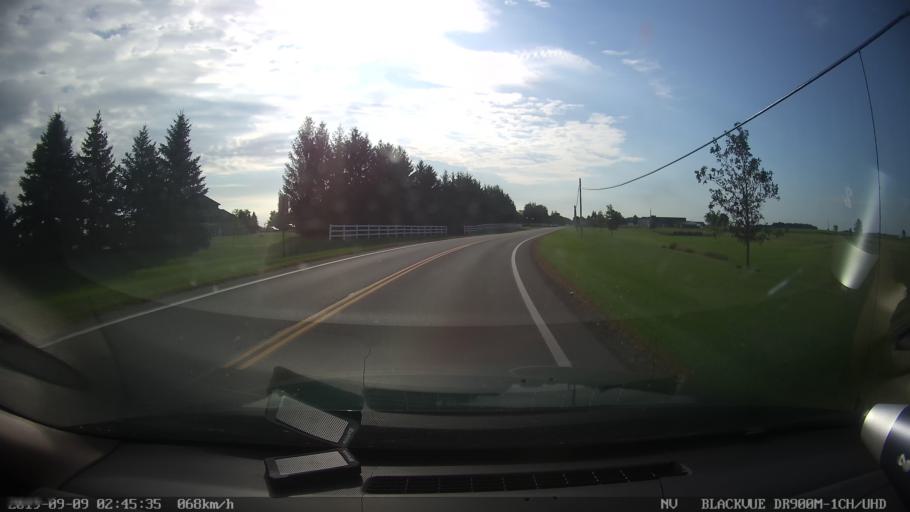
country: US
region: Ohio
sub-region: Crawford County
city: Bucyrus
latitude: 40.7934
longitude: -82.9520
